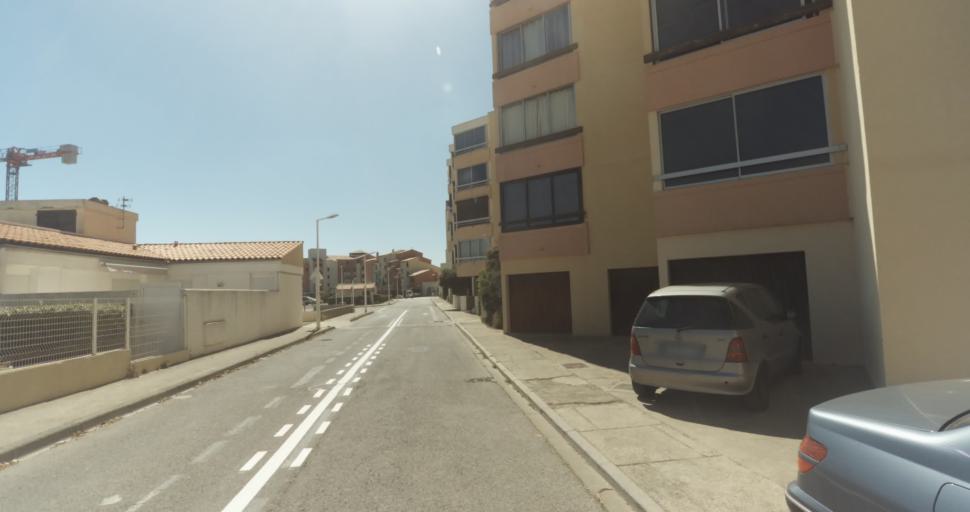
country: FR
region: Languedoc-Roussillon
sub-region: Departement de l'Aude
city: Leucate
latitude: 42.8607
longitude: 3.0386
